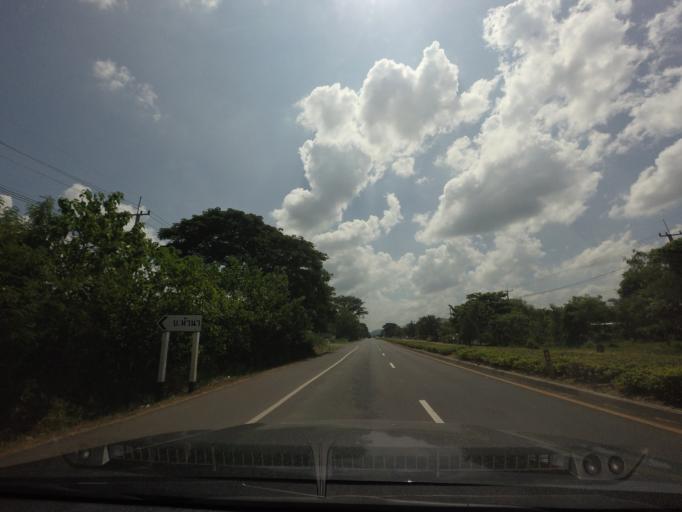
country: TH
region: Phetchabun
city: Phetchabun
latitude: 16.2798
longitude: 101.0608
